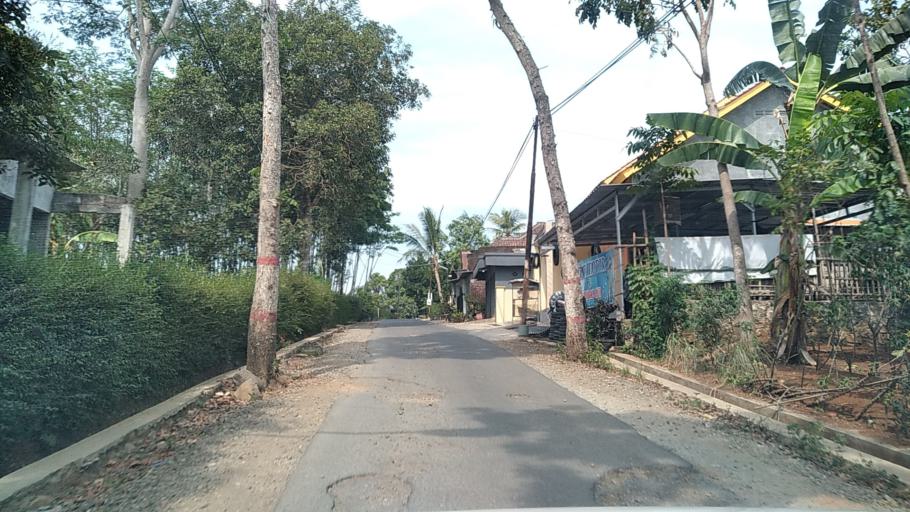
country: ID
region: Central Java
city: Ungaran
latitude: -7.0560
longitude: 110.3101
